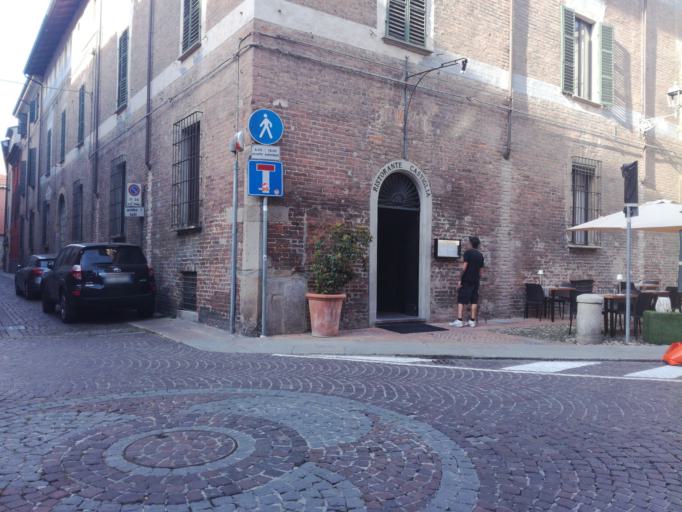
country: IT
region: Emilia-Romagna
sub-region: Provincia di Piacenza
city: Piacenza
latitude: 45.0505
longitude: 9.6923
